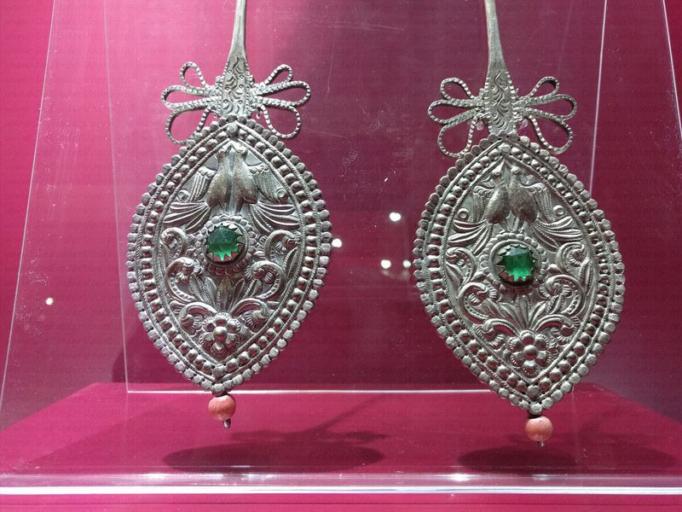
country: BO
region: Chuquisaca
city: Sucre
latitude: -19.0478
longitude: -65.2575
